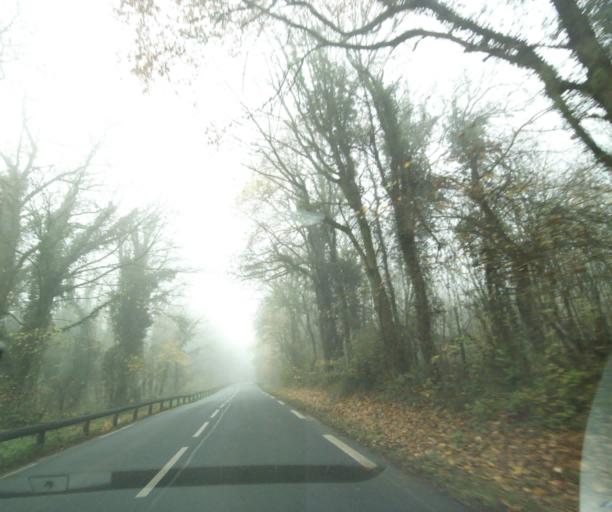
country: FR
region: Ile-de-France
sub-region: Departement de Seine-Saint-Denis
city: Coubron
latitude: 48.9253
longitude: 2.5864
